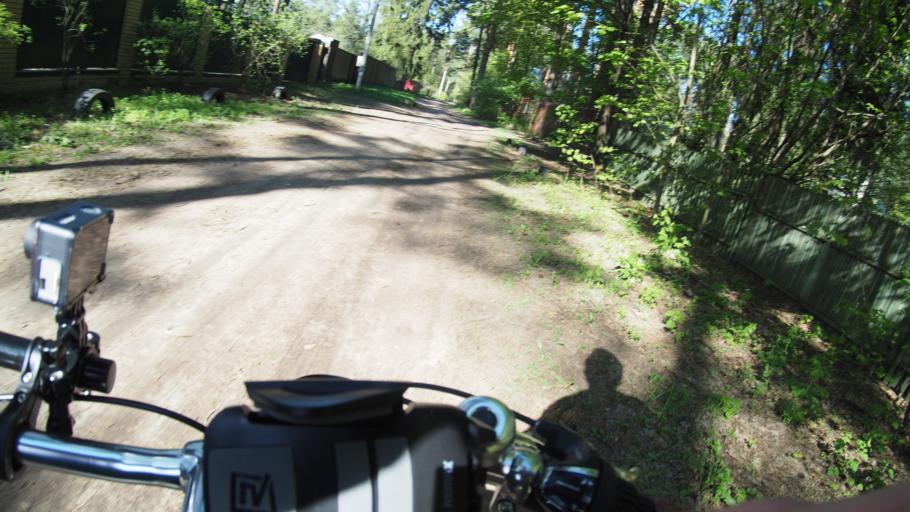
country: RU
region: Moskovskaya
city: Kratovo
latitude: 55.5883
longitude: 38.1841
